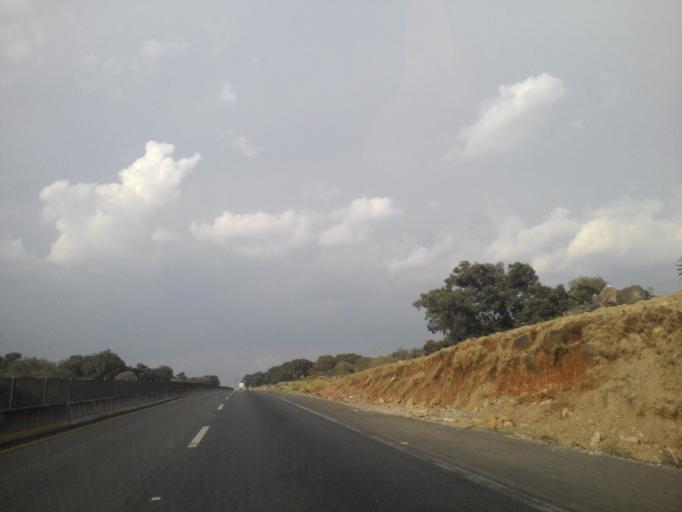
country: MX
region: Jalisco
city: Tepatitlan de Morelos
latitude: 20.8516
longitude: -102.7748
